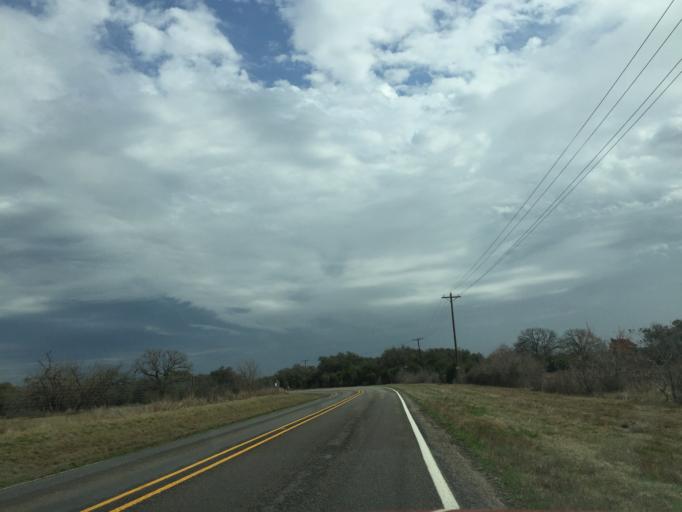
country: US
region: Texas
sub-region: Burnet County
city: Bertram
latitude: 30.6522
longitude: -97.9687
